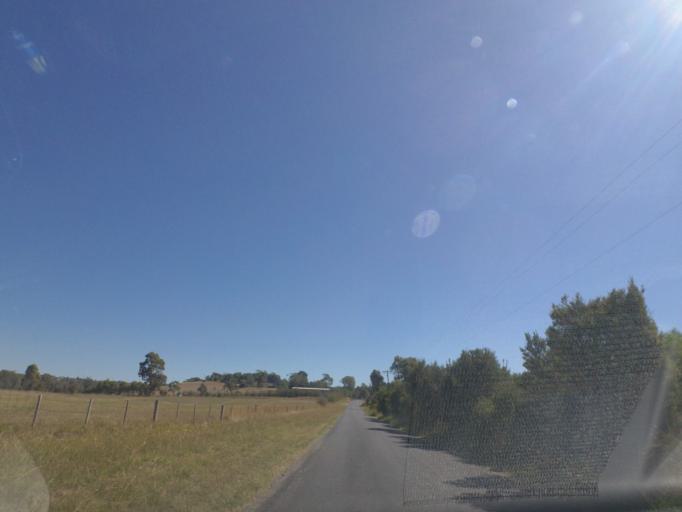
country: AU
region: Victoria
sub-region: Yarra Ranges
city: Chirnside Park
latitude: -37.7287
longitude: 145.2907
